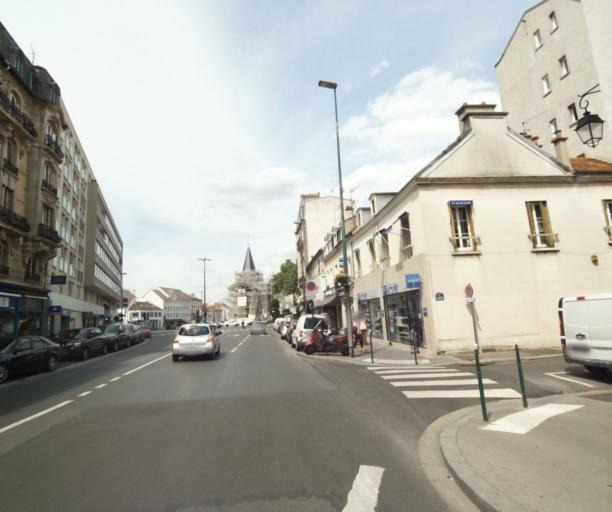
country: FR
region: Ile-de-France
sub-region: Departement des Hauts-de-Seine
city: Colombes
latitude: 48.9222
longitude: 2.2527
